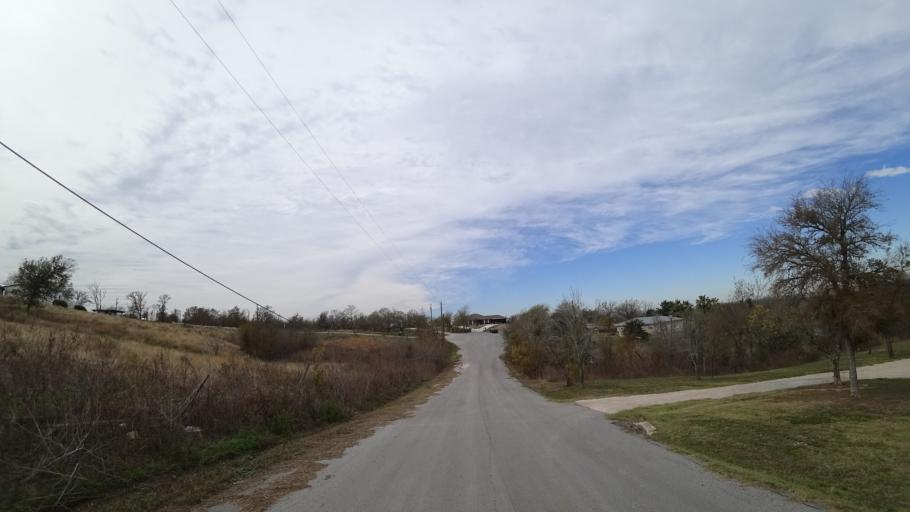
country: US
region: Texas
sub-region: Travis County
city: Garfield
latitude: 30.1471
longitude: -97.5874
